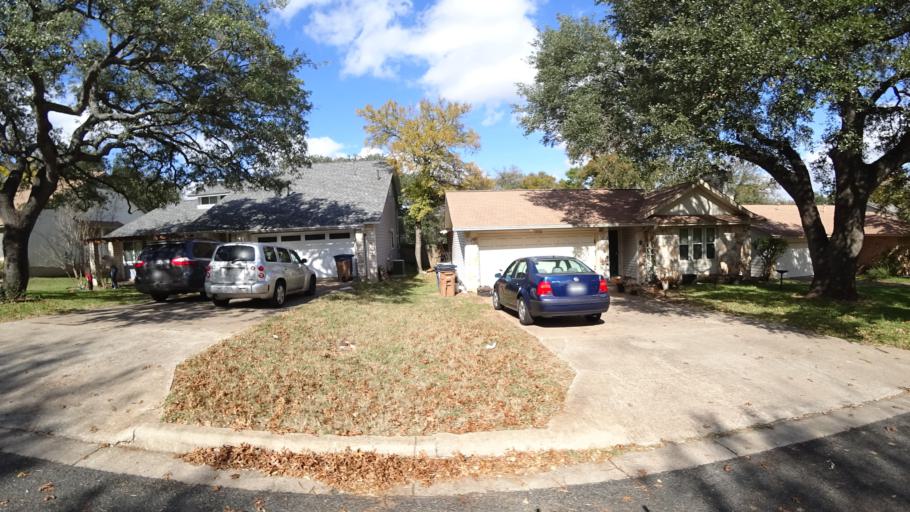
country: US
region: Texas
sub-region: Travis County
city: Wells Branch
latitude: 30.4234
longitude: -97.7247
